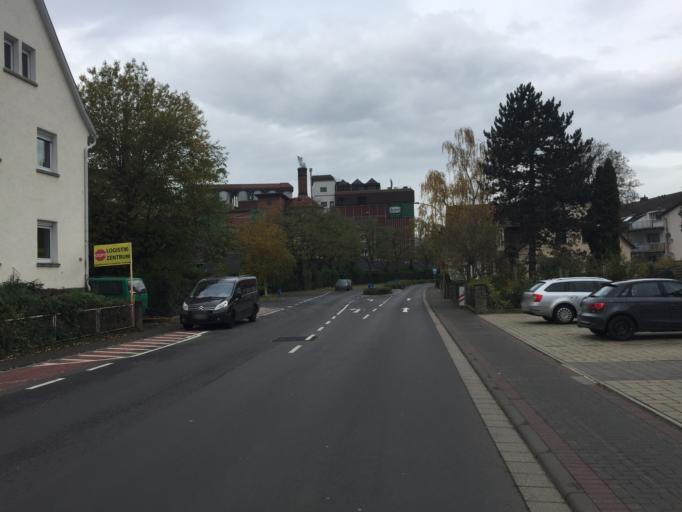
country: DE
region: Hesse
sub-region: Regierungsbezirk Giessen
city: Lich
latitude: 50.5142
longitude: 8.8198
